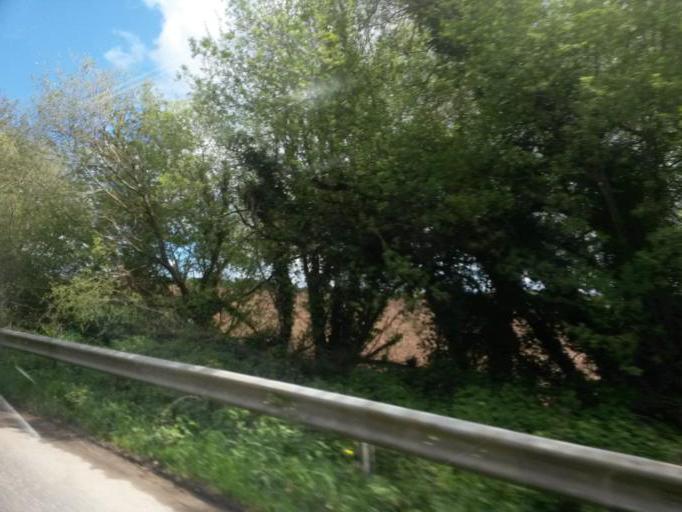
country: IE
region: Leinster
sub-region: Loch Garman
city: Enniscorthy
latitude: 52.4545
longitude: -6.5554
